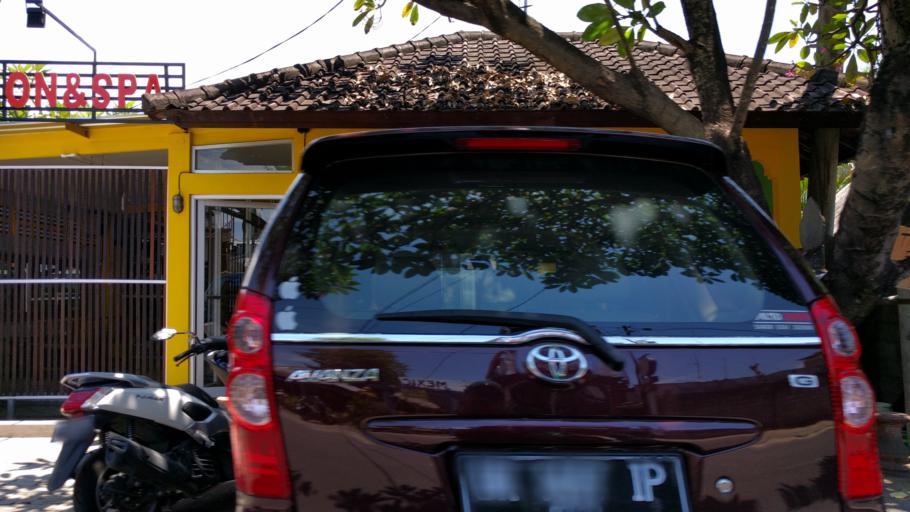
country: ID
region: Bali
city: Banjar Medura
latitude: -8.7051
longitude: 115.2579
